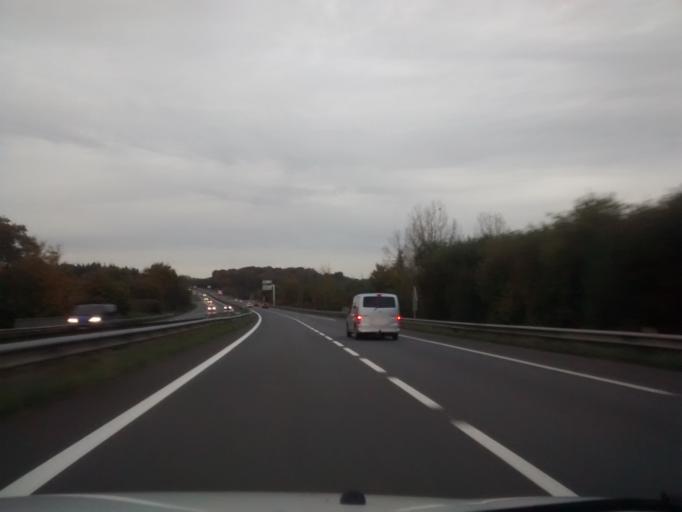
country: FR
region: Brittany
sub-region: Departement d'Ille-et-Vilaine
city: Quedillac
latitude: 48.2660
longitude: -2.1482
